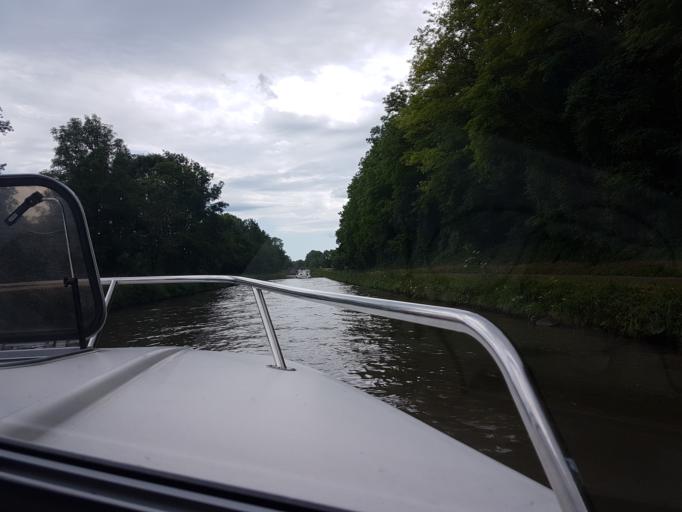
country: FR
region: Bourgogne
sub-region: Departement de la Nievre
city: Clamecy
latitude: 47.4859
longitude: 3.5243
